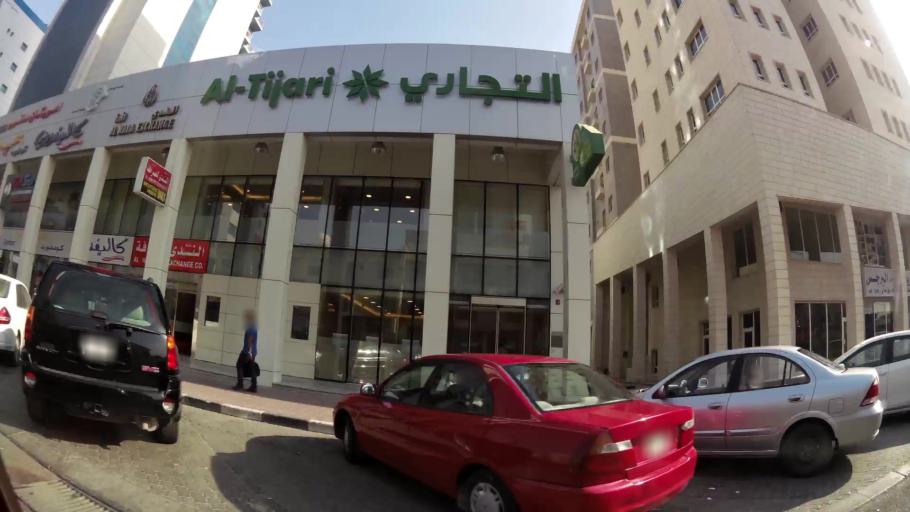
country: KW
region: Muhafazat Hawalli
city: Hawalli
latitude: 29.3414
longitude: 48.0198
